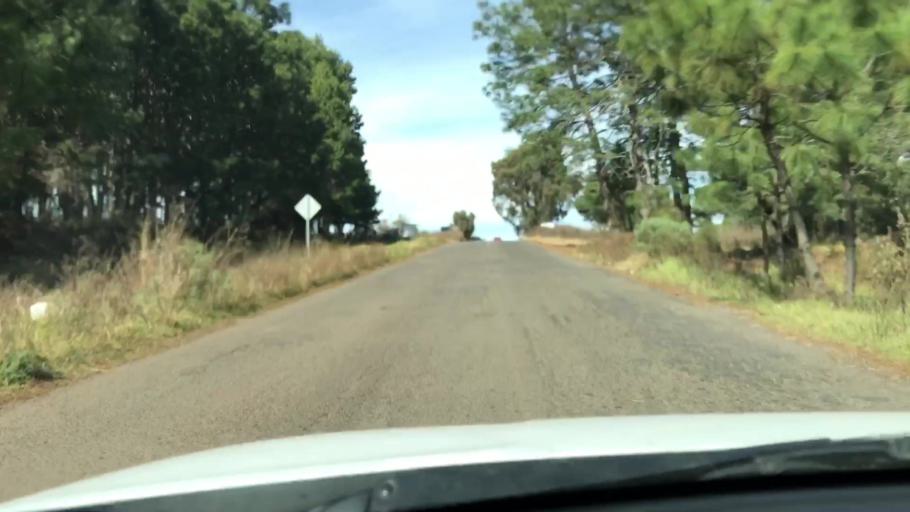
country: MX
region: Jalisco
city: Chiquilistlan
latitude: 20.1212
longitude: -103.7235
